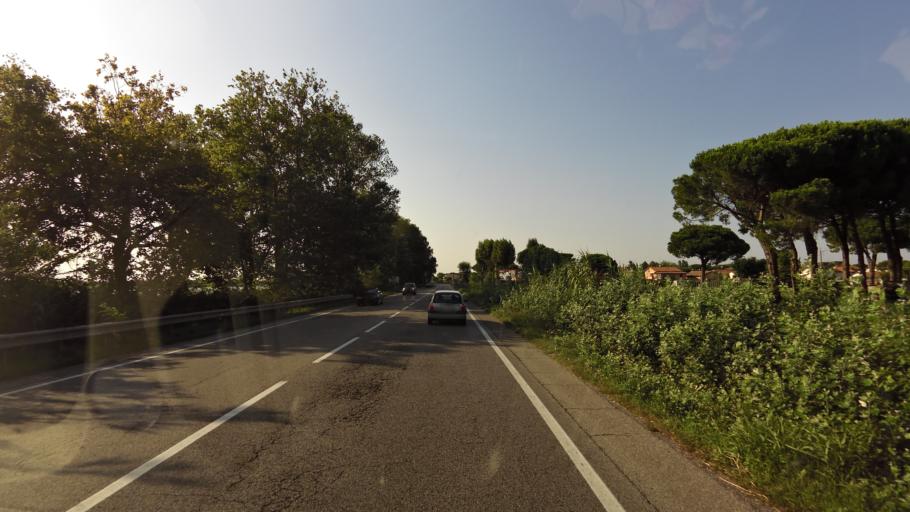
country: IT
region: Emilia-Romagna
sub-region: Provincia di Ravenna
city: Cervia
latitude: 44.2476
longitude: 12.3488
